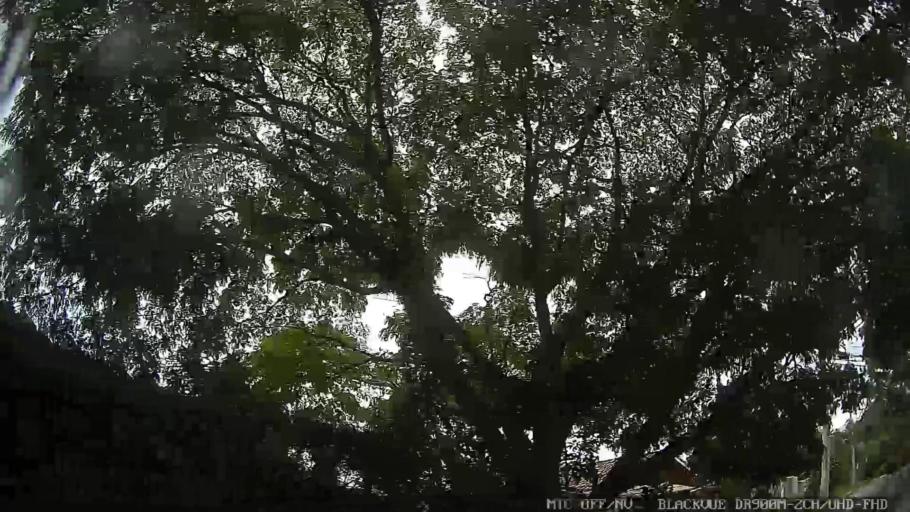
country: BR
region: Sao Paulo
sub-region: Serra Negra
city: Serra Negra
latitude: -22.6147
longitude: -46.7167
